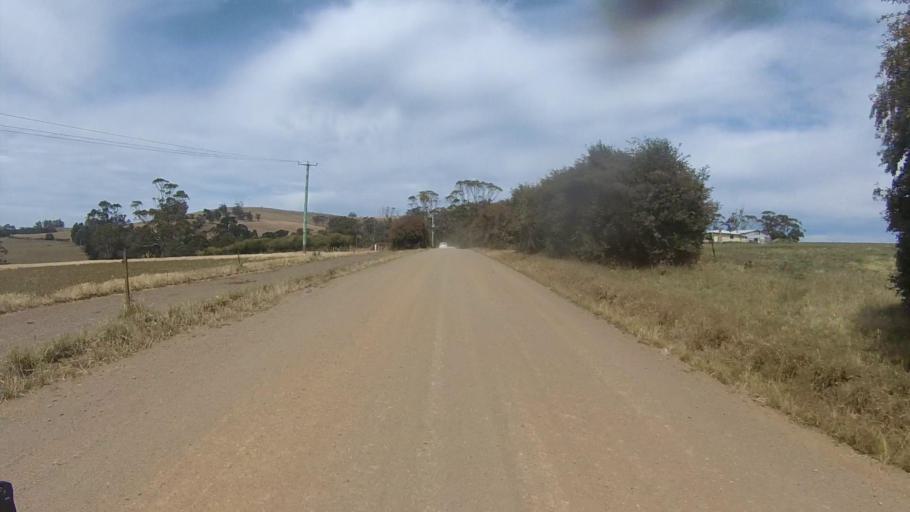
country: AU
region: Tasmania
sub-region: Sorell
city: Sorell
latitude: -42.8171
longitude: 147.8250
